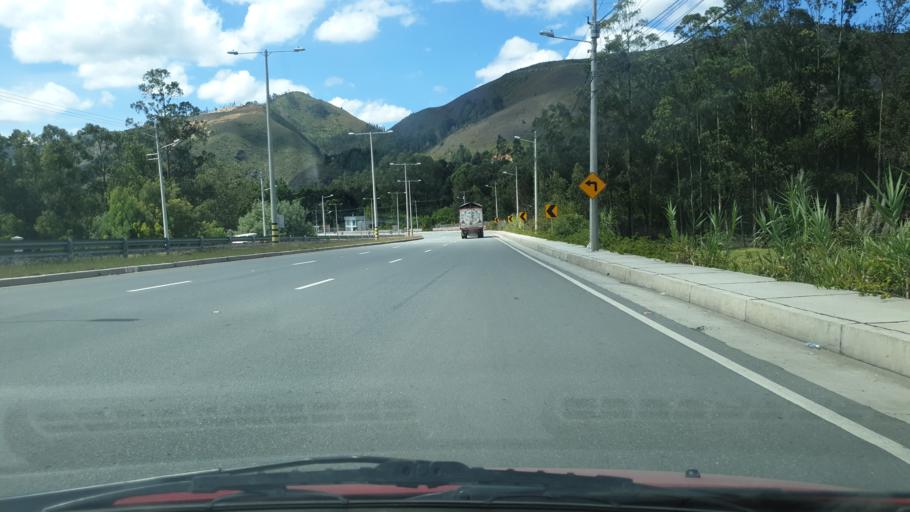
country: EC
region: Azuay
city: Llacao
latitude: -2.8442
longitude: -78.8803
